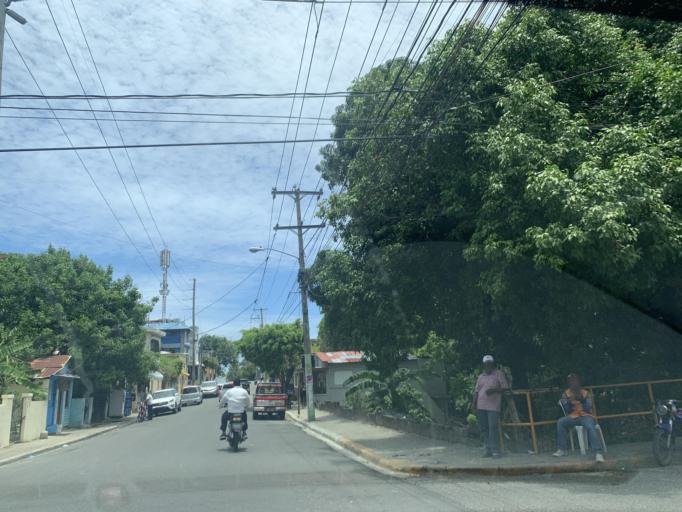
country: DO
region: Puerto Plata
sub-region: Puerto Plata
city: Puerto Plata
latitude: 19.7914
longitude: -70.6844
